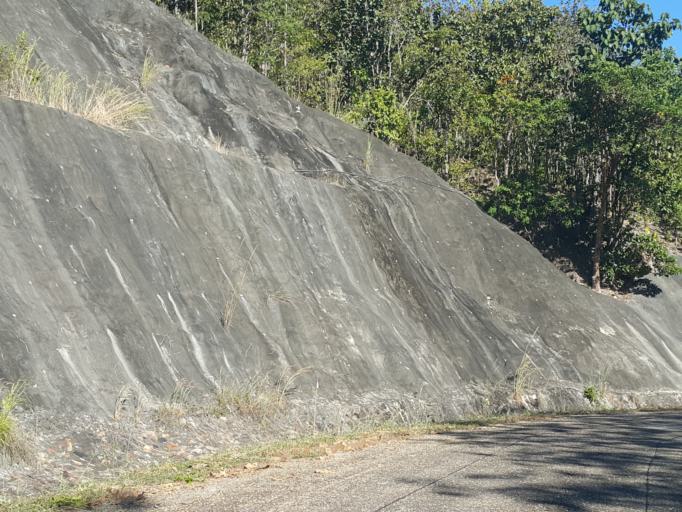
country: TH
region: Chiang Mai
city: San Sai
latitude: 18.9282
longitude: 99.1287
